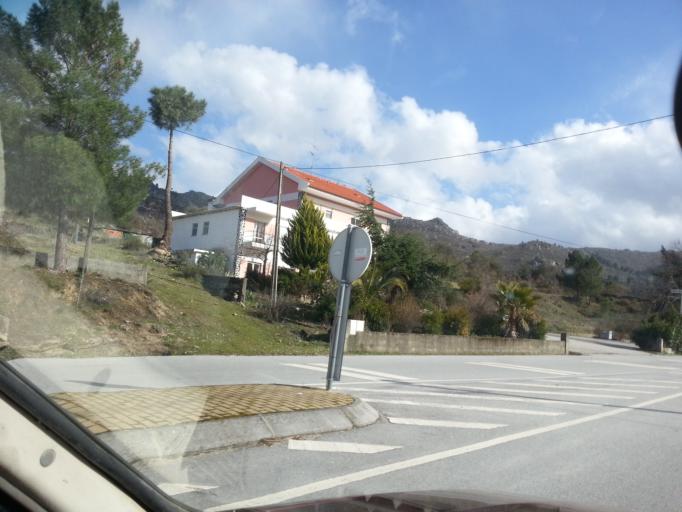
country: PT
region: Guarda
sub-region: Guarda
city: Guarda
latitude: 40.5980
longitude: -7.2907
